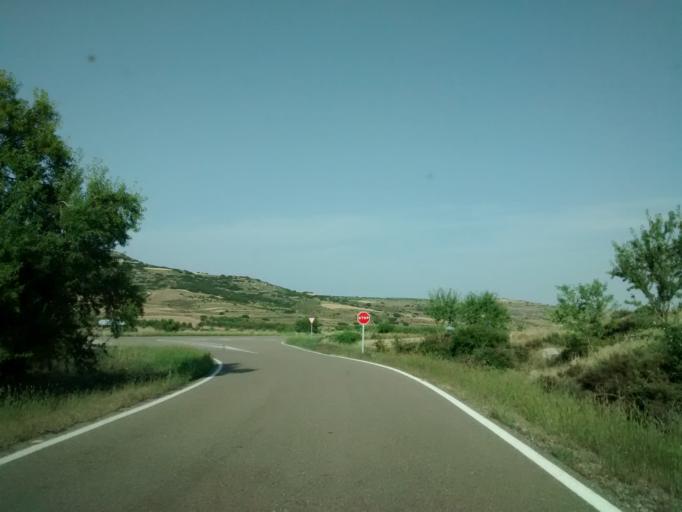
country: ES
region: Aragon
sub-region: Provincia de Zaragoza
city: Trasmoz
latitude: 41.8439
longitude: -1.7226
